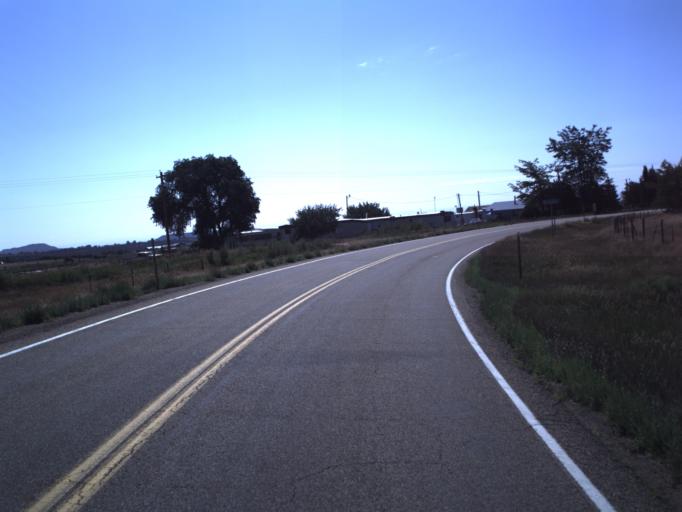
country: US
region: Utah
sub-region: Duchesne County
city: Duchesne
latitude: 40.3589
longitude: -110.2762
